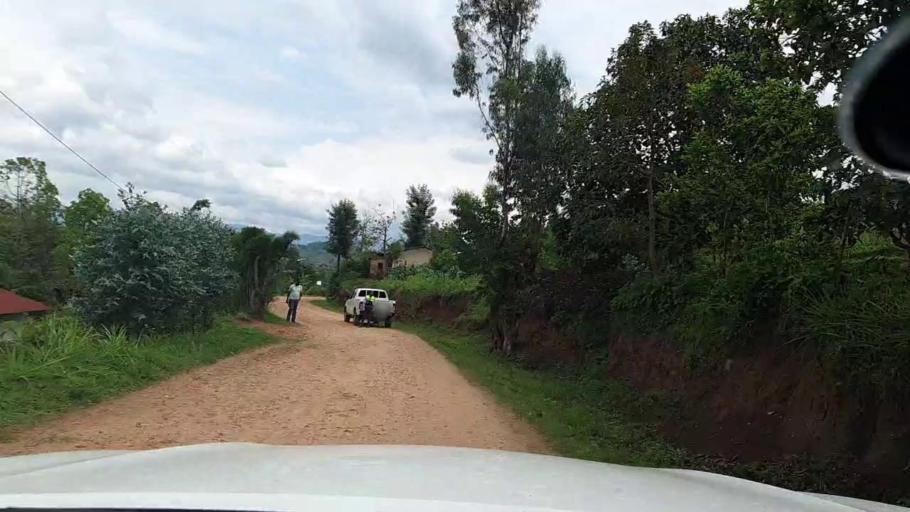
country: RW
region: Western Province
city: Kibuye
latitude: -2.0740
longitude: 29.4238
